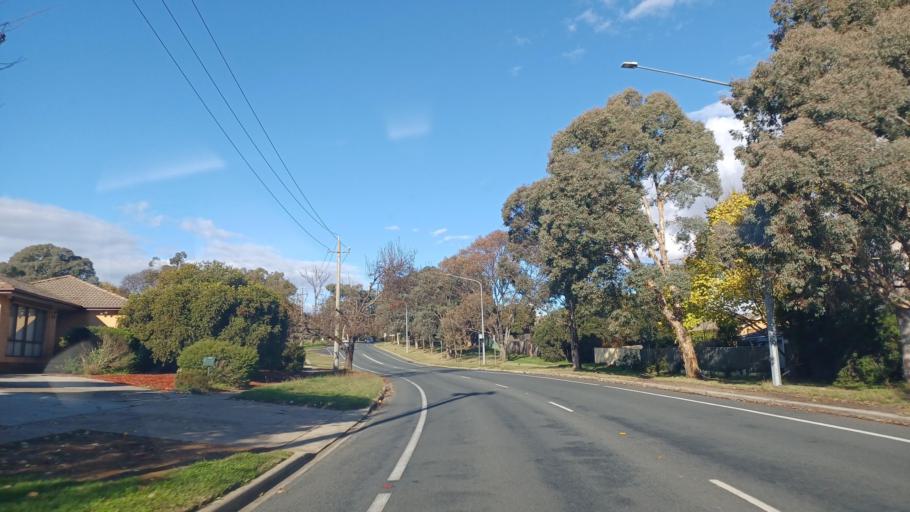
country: AU
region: Australian Capital Territory
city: Belconnen
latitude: -35.1968
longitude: 149.0423
